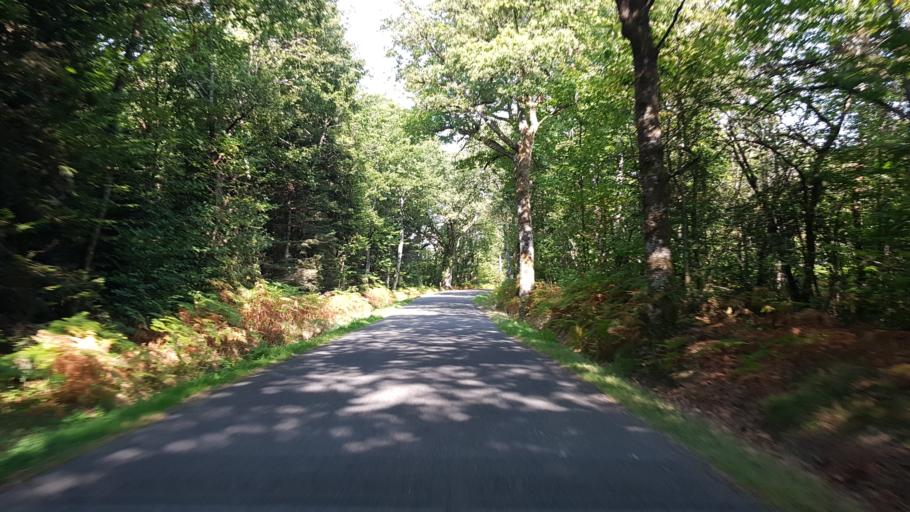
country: FR
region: Poitou-Charentes
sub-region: Departement de la Charente
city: Etagnac
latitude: 45.9199
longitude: 0.7898
